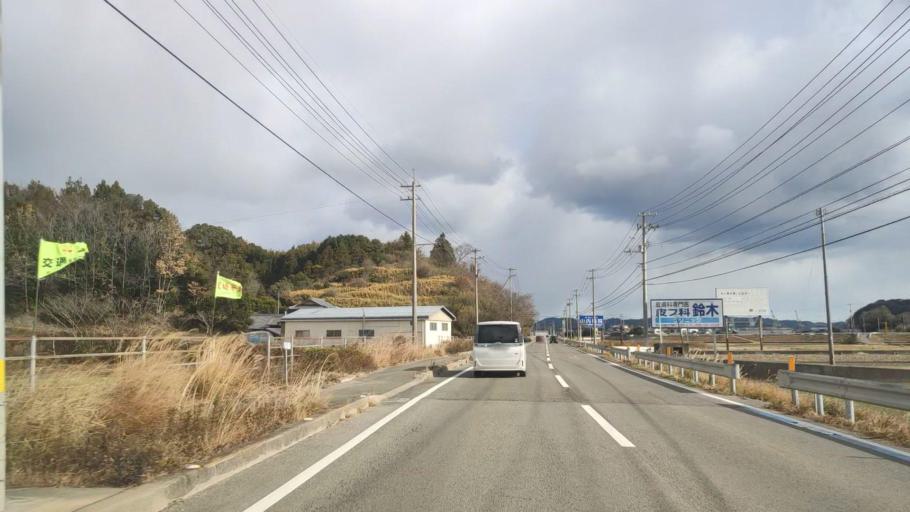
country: JP
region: Ehime
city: Hojo
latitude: 34.0614
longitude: 132.8942
